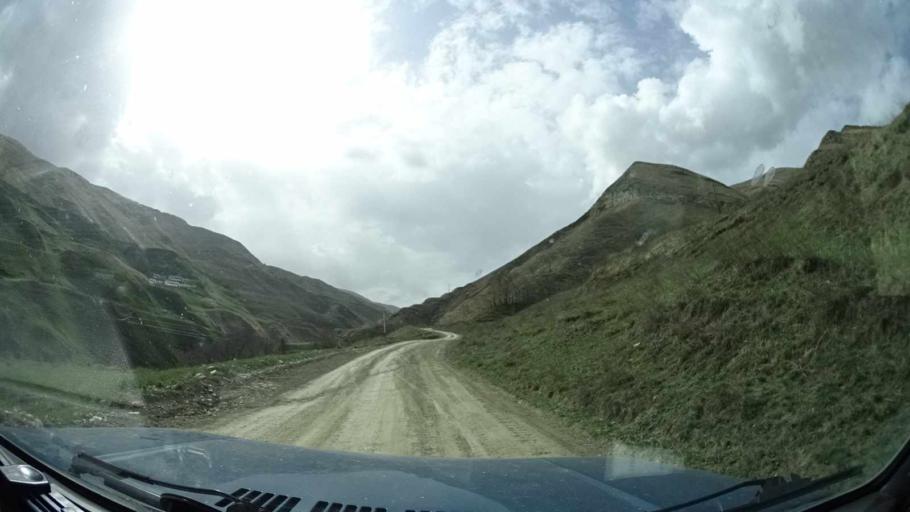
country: RU
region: Dagestan
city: Usisha
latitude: 42.1246
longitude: 47.3823
